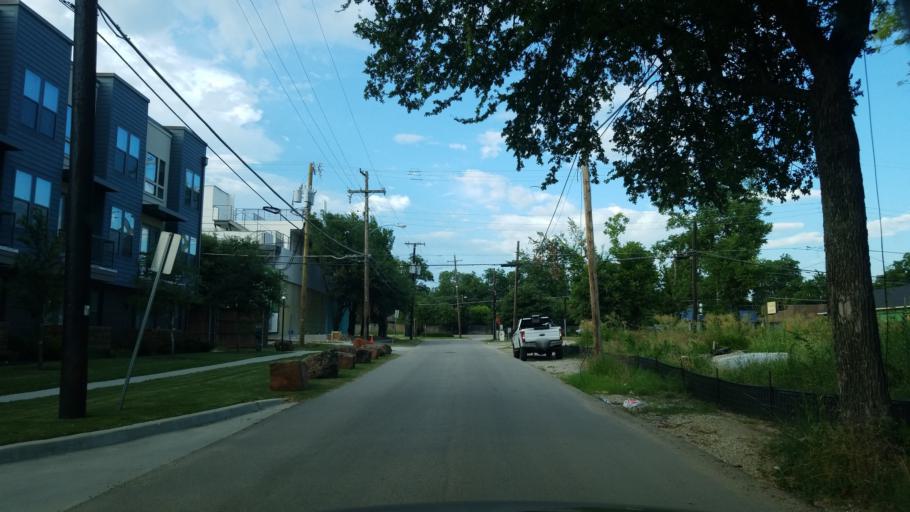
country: US
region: Texas
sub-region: Dallas County
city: Highland Park
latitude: 32.8120
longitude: -96.7770
